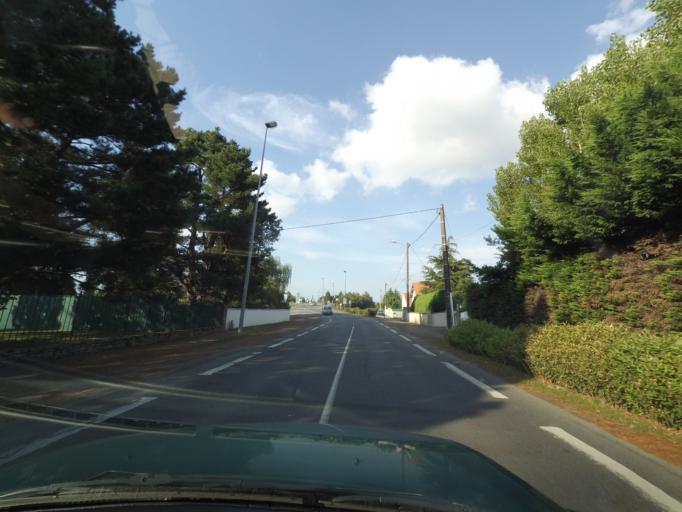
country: FR
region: Pays de la Loire
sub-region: Departement de la Loire-Atlantique
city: Saint-Philbert-de-Grand-Lieu
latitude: 47.0455
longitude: -1.6388
